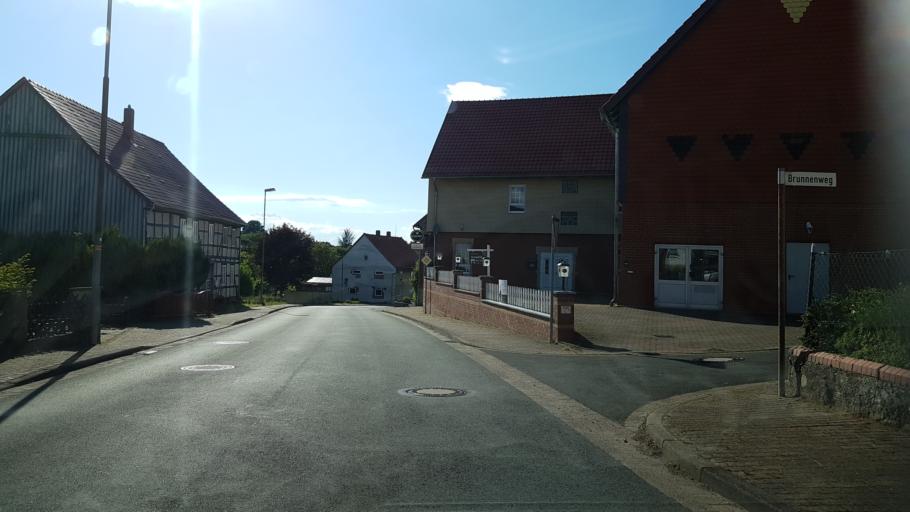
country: DE
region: Lower Saxony
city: Coppengrave
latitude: 51.9680
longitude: 9.7672
